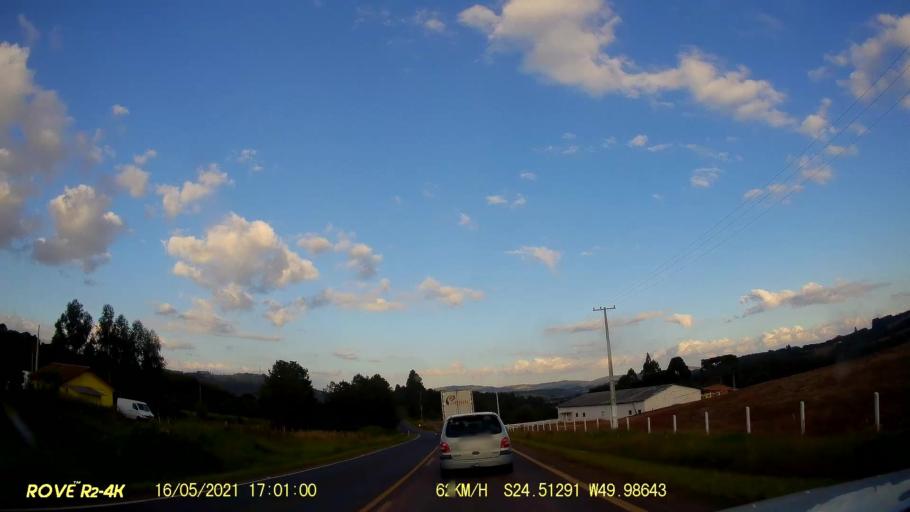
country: BR
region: Parana
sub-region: Pirai Do Sul
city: Pirai do Sul
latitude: -24.5130
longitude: -49.9863
